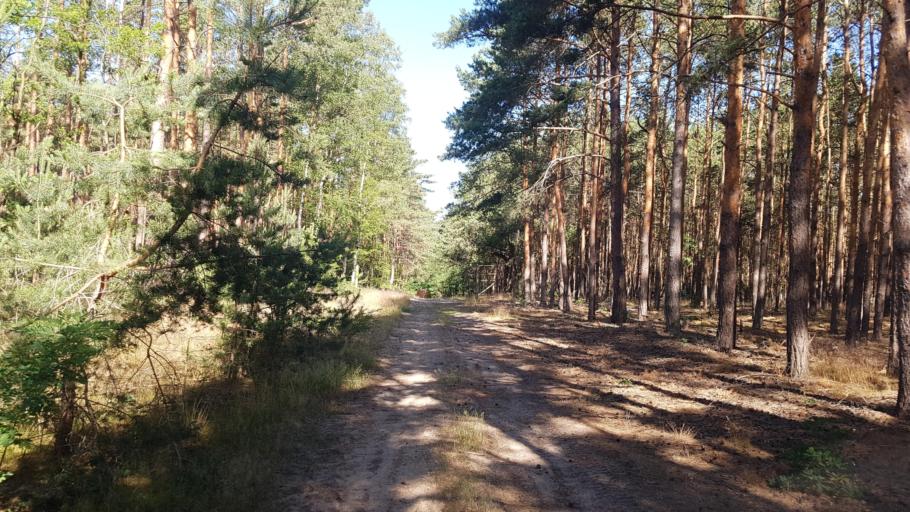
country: DE
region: Brandenburg
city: Juterbog
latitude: 51.9794
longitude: 13.1367
